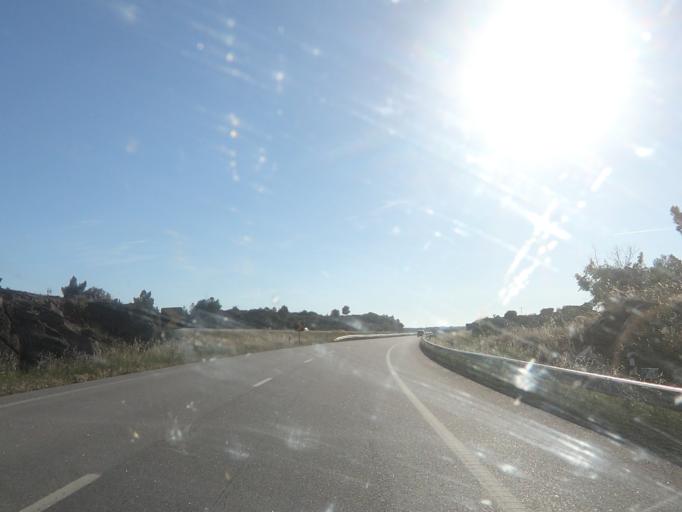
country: ES
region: Castille and Leon
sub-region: Provincia de Salamanca
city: Fuentes de Onoro
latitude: 40.6130
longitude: -6.8905
